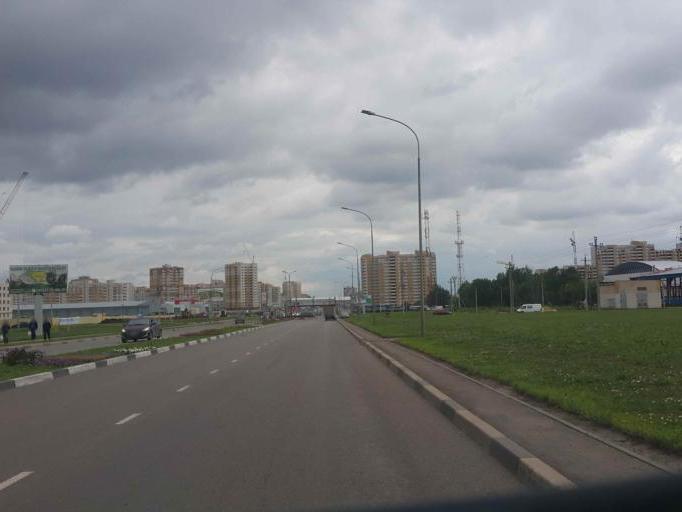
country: RU
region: Tambov
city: Tambov
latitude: 52.7697
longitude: 41.3905
